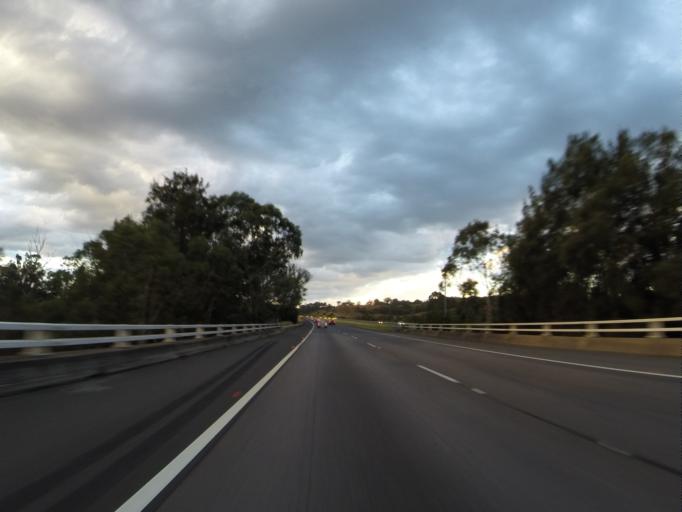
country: AU
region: New South Wales
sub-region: Campbelltown Municipality
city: Glen Alpine
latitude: -34.1194
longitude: 150.7565
